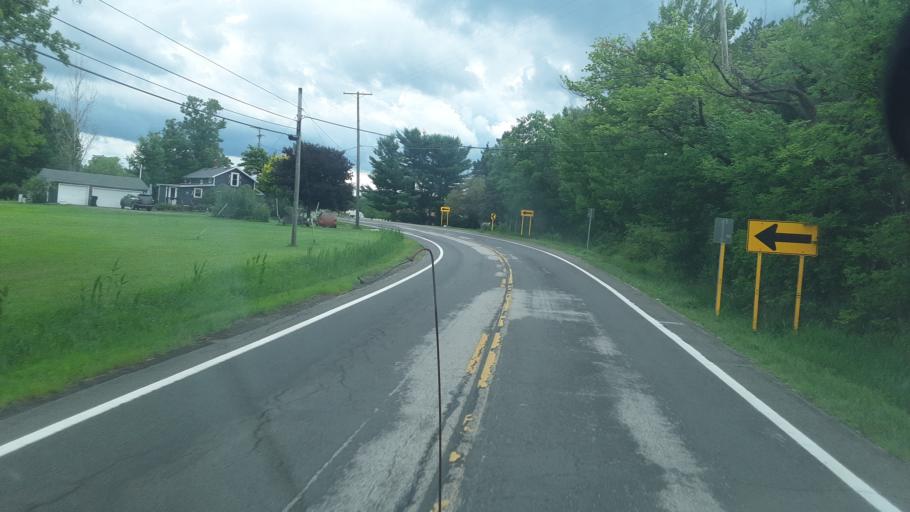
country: US
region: Ohio
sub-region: Ashtabula County
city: Jefferson
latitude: 41.7151
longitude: -80.7805
